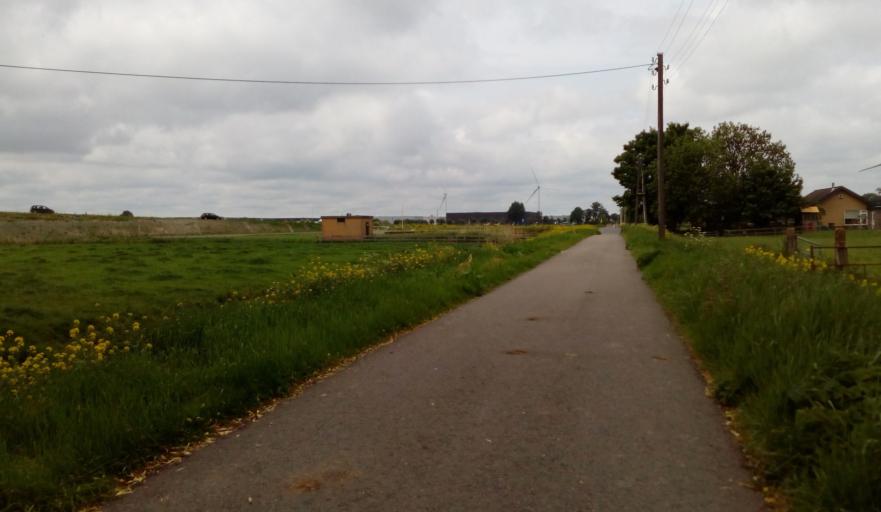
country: NL
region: South Holland
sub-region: Gemeente Waddinxveen
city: Waddinxveen
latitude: 52.0105
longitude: 4.6483
